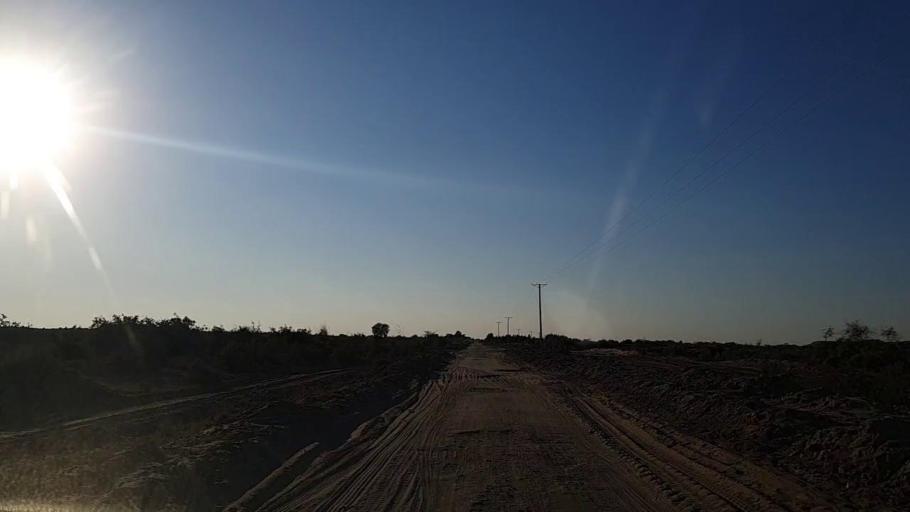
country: PK
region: Sindh
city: Khadro
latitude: 26.2790
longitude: 68.8724
